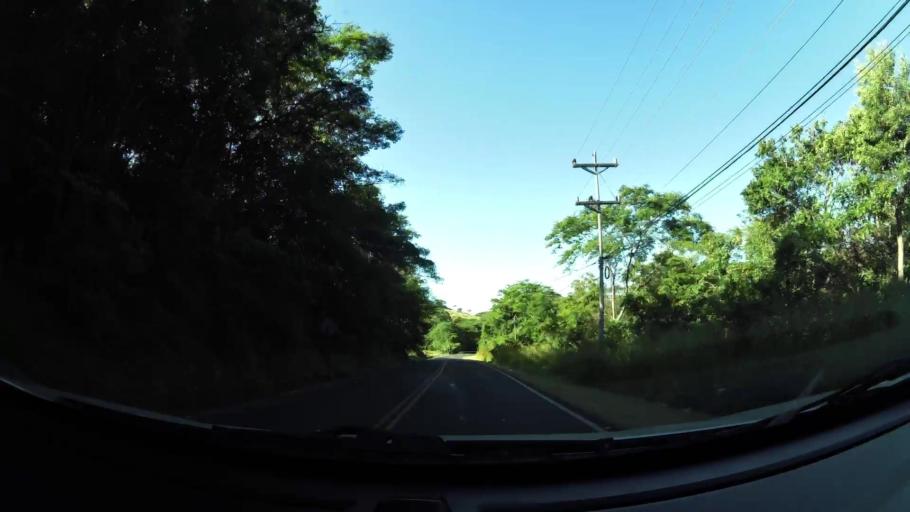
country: CR
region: Guanacaste
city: Belen
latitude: 10.3742
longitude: -85.6255
